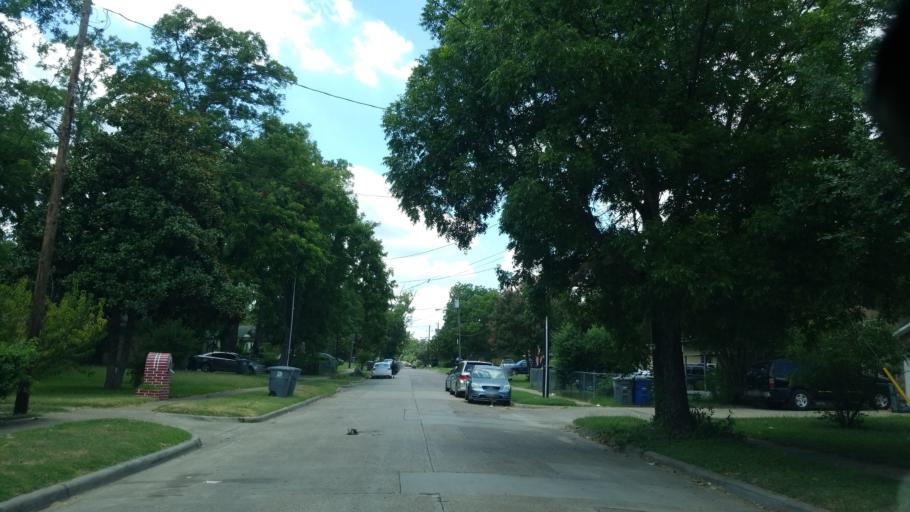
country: US
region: Texas
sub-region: Dallas County
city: Dallas
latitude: 32.7410
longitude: -96.7488
